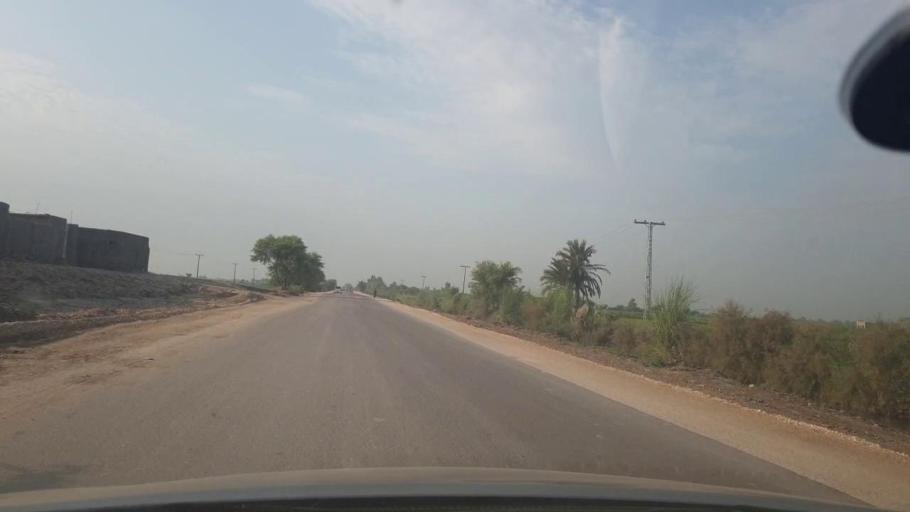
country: PK
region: Sindh
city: Jacobabad
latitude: 28.2114
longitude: 68.3685
